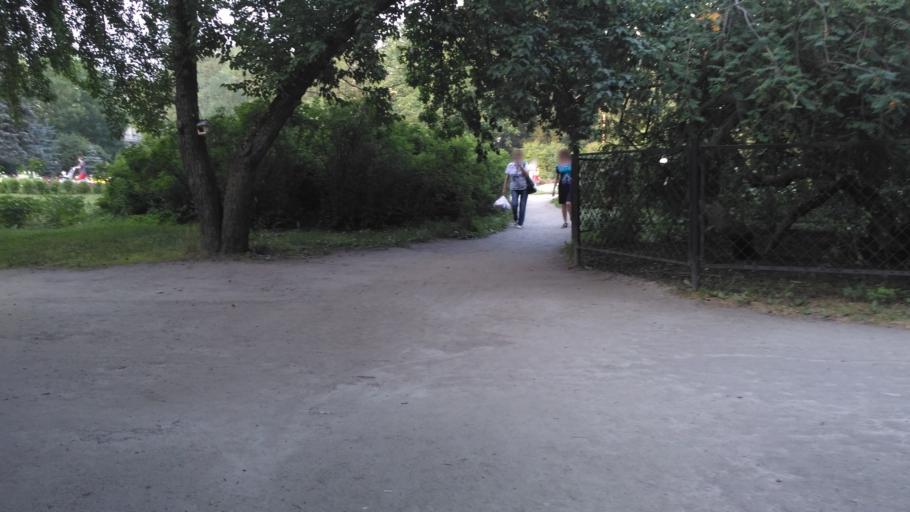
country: RU
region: Sverdlovsk
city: Yekaterinburg
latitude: 56.8475
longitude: 60.6522
